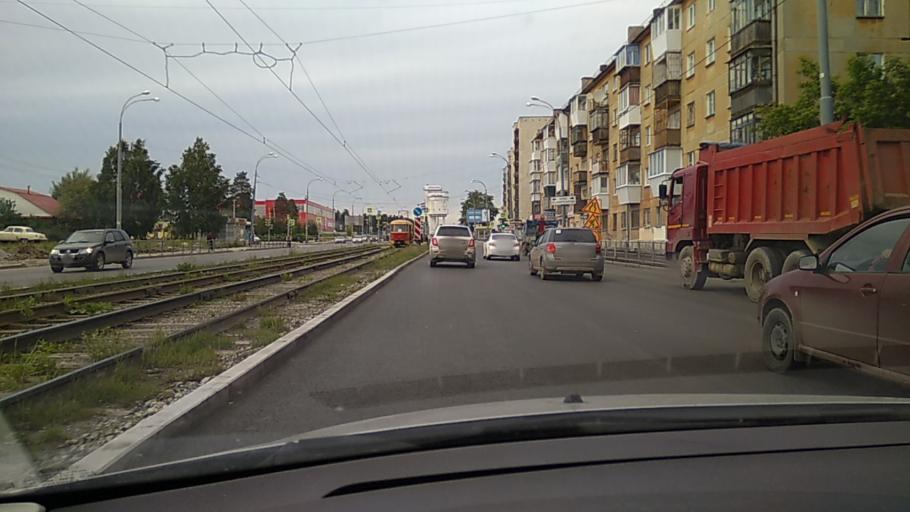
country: RU
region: Sverdlovsk
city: Yekaterinburg
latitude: 56.8897
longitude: 60.5686
